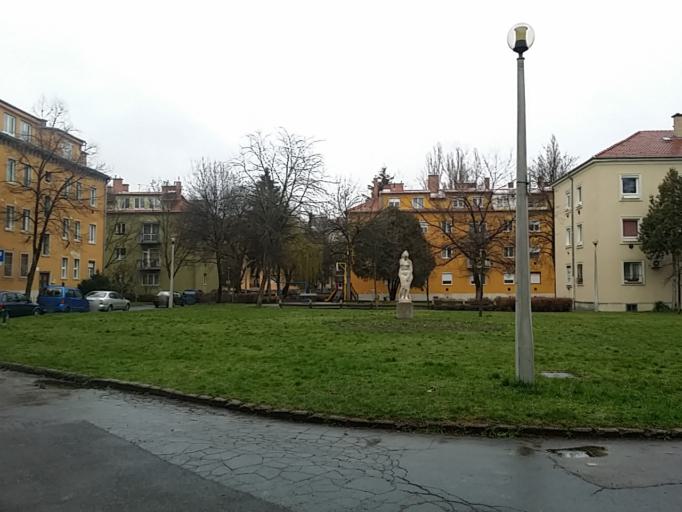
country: HU
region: Heves
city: Eger
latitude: 47.9000
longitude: 20.3794
